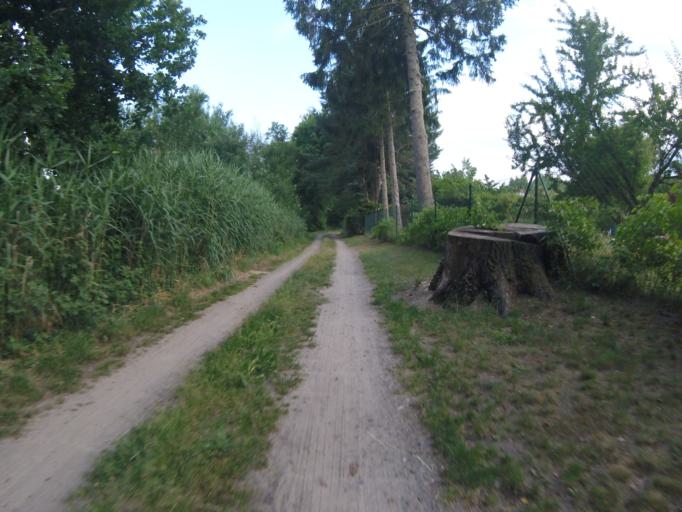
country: DE
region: Brandenburg
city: Bestensee
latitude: 52.2711
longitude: 13.6363
